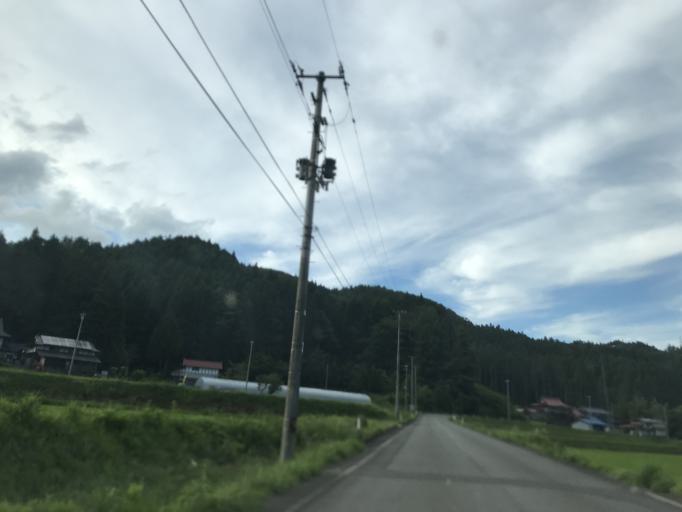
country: JP
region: Iwate
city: Ichinoseki
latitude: 38.9000
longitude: 140.9790
